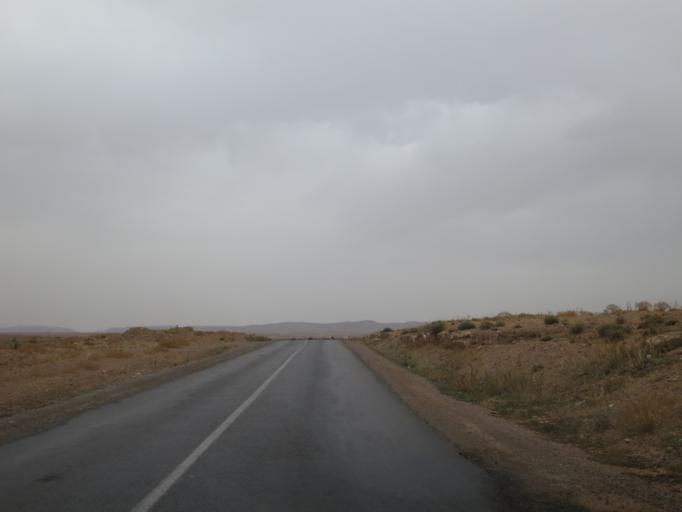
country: MA
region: Meknes-Tafilalet
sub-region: Khenifra
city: Midelt
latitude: 32.6982
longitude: -4.8174
